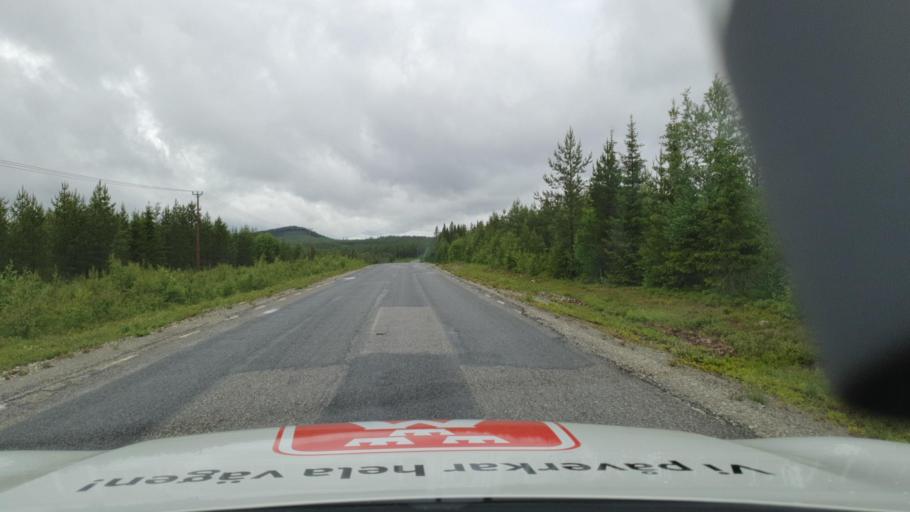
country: SE
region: Vaesterbotten
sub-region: Dorotea Kommun
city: Dorotea
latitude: 64.1504
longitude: 16.6506
